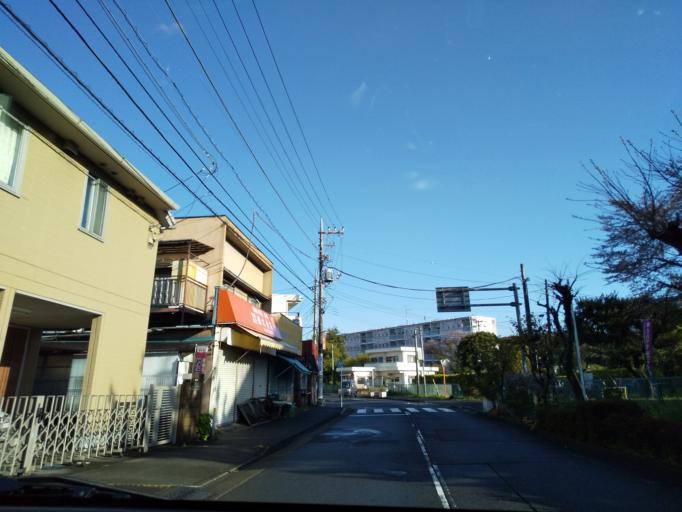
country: JP
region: Tokyo
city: Hino
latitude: 35.6484
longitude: 139.3768
